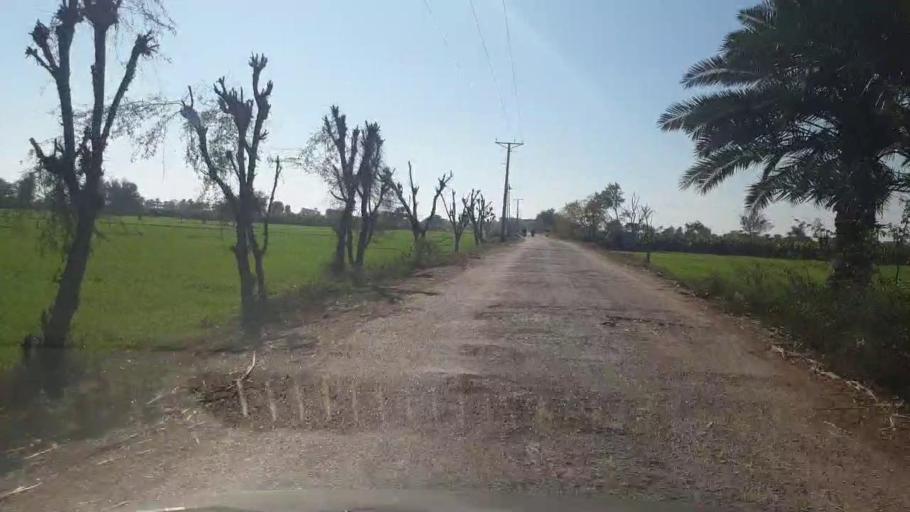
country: PK
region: Sindh
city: Bozdar
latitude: 27.2549
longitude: 68.6524
